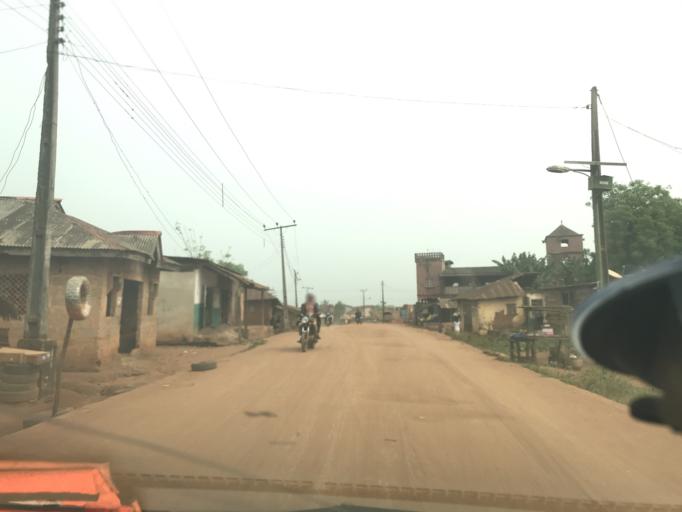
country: NG
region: Ogun
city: Ado Odo
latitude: 6.5883
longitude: 2.9339
